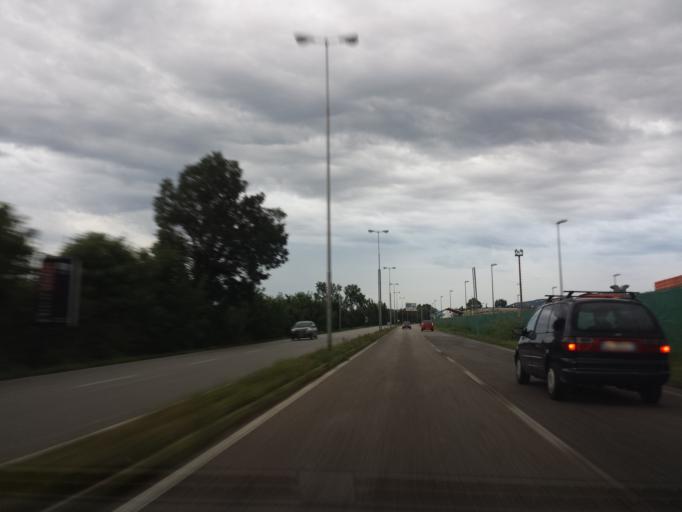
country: IT
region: Veneto
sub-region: Provincia di Vicenza
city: Villaggio Montegrappa
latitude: 45.5481
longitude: 11.5843
